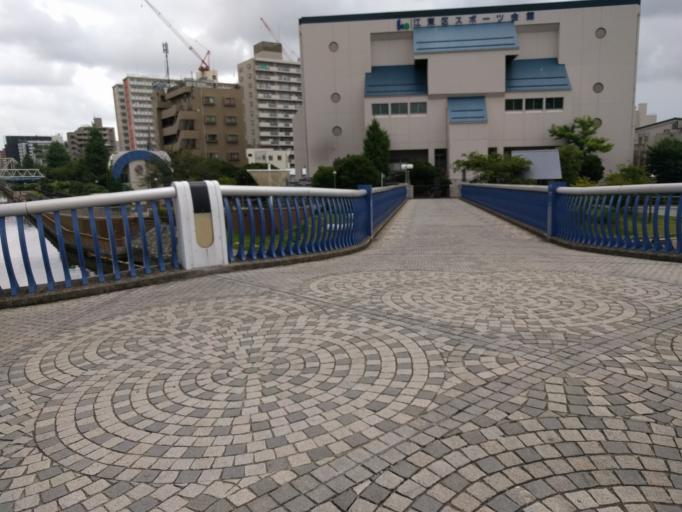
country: JP
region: Tokyo
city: Urayasu
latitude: 35.6851
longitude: 139.8207
